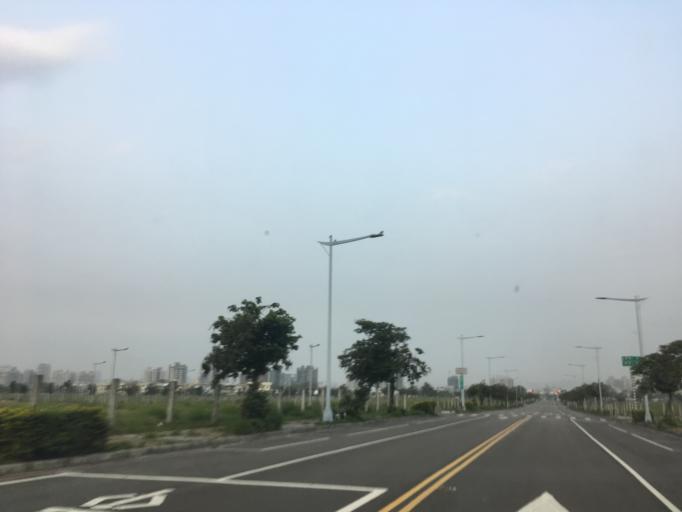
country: TW
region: Taiwan
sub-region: Taichung City
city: Taichung
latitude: 24.1967
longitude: 120.6761
